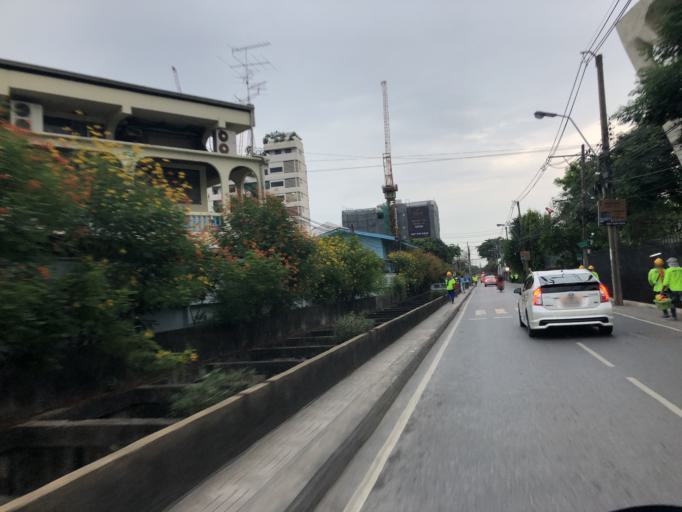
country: TH
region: Bangkok
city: Khlong Toei
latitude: 13.7186
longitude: 100.5807
